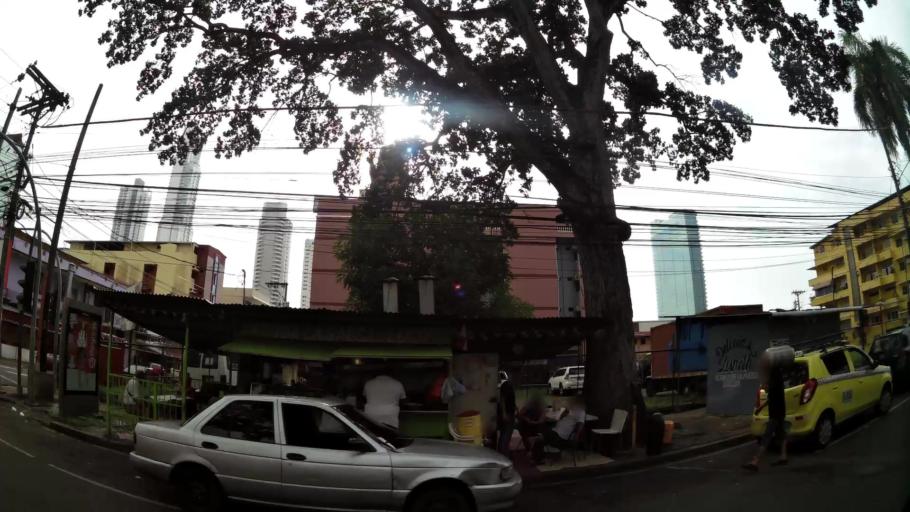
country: PA
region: Panama
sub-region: Distrito de Panama
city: Ancon
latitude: 8.9670
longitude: -79.5374
